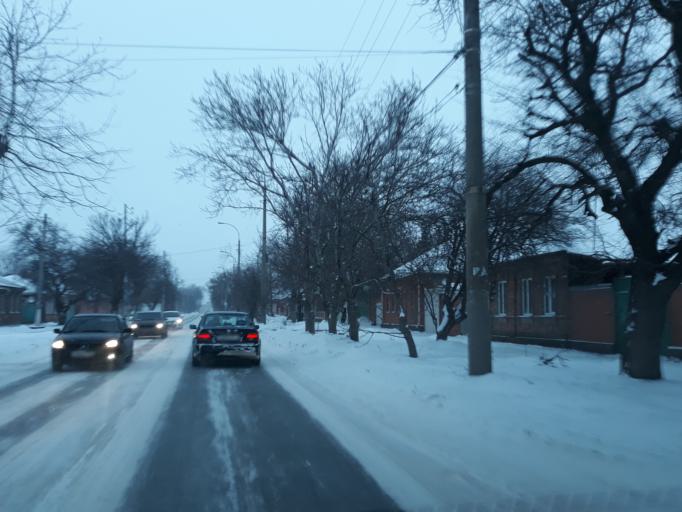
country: RU
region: Rostov
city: Taganrog
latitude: 47.2553
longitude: 38.9384
